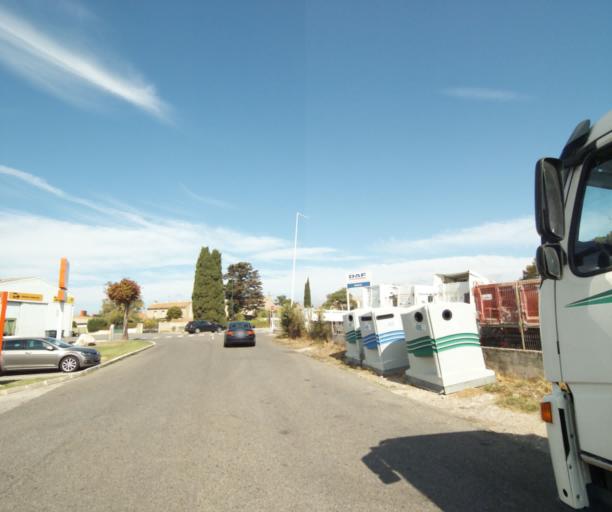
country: FR
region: Provence-Alpes-Cote d'Azur
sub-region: Departement des Bouches-du-Rhone
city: Saint-Victoret
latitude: 43.4188
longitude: 5.2305
